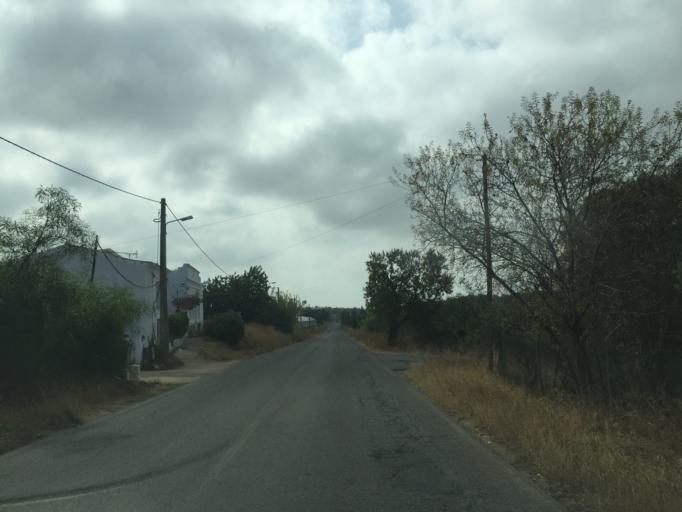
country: PT
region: Faro
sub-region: Olhao
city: Olhao
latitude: 37.0690
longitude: -7.8818
